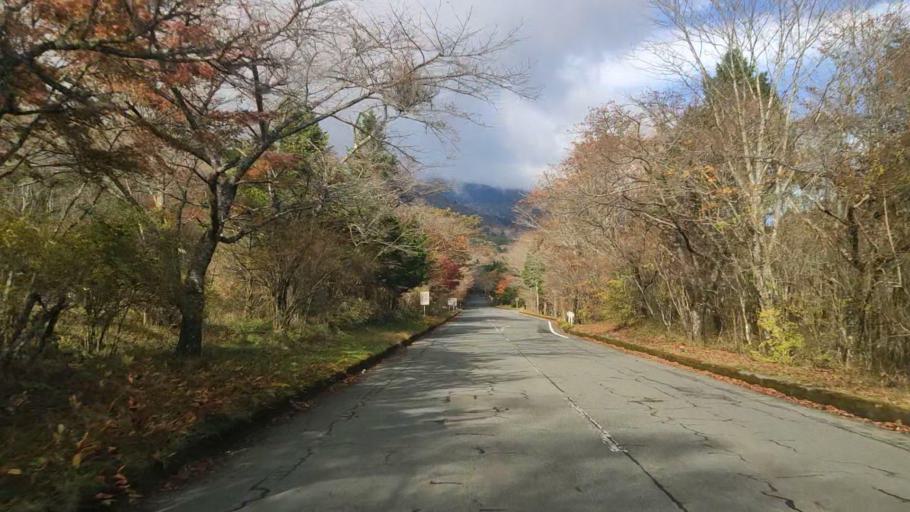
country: JP
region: Shizuoka
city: Fujinomiya
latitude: 35.2962
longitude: 138.7154
